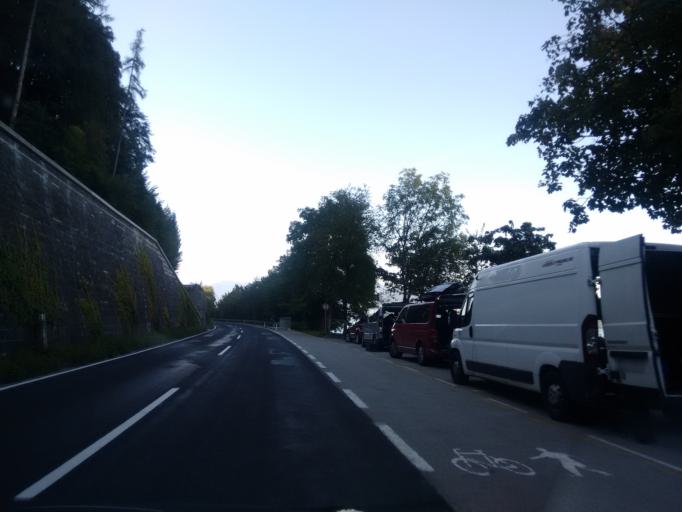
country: AT
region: Upper Austria
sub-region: Politischer Bezirk Vocklabruck
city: Steinbach am Attersee
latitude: 47.8673
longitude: 13.5654
